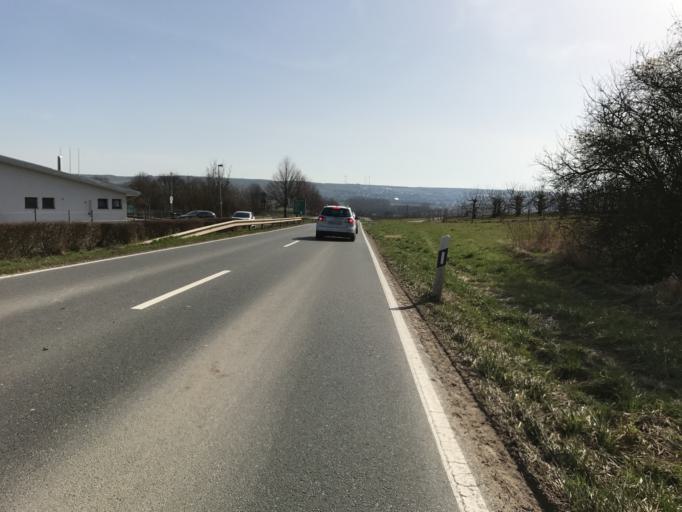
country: DE
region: Rheinland-Pfalz
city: Essenheim
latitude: 49.9249
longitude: 8.1654
